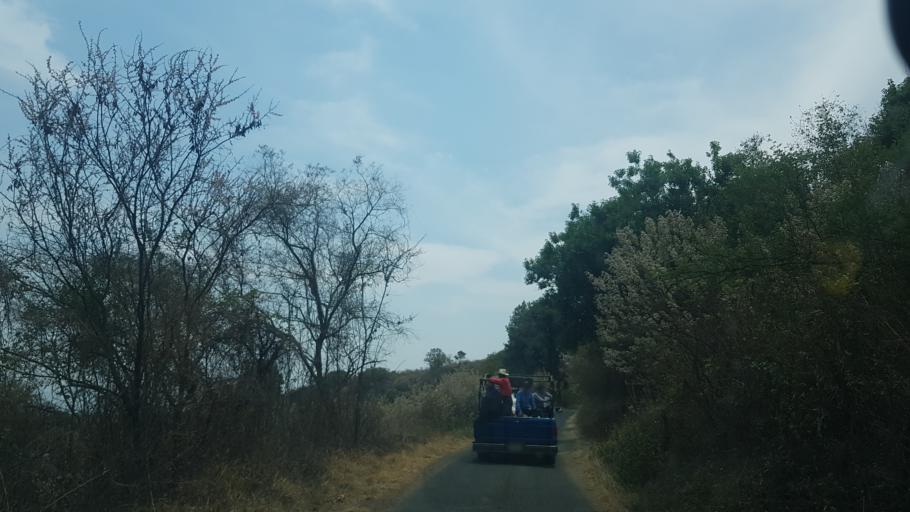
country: MX
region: Puebla
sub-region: Atzitzihuacan
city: Santiago Atzitzihuacan
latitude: 18.8482
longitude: -98.6093
